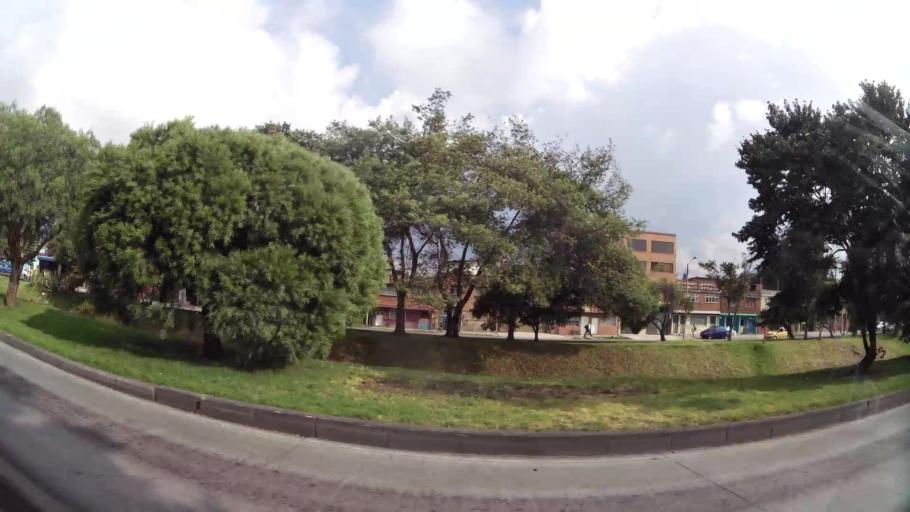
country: CO
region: Bogota D.C.
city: Bogota
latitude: 4.5695
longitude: -74.1330
